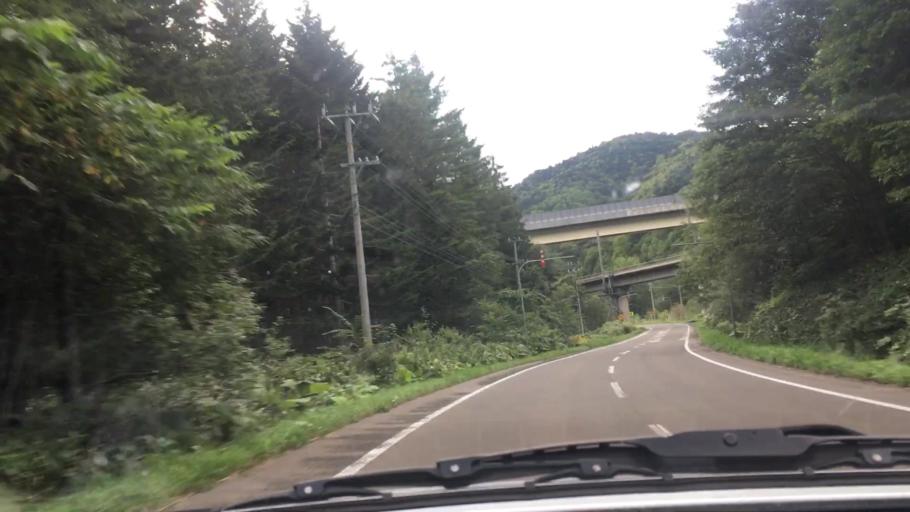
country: JP
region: Hokkaido
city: Shimo-furano
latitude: 43.0506
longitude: 142.4977
